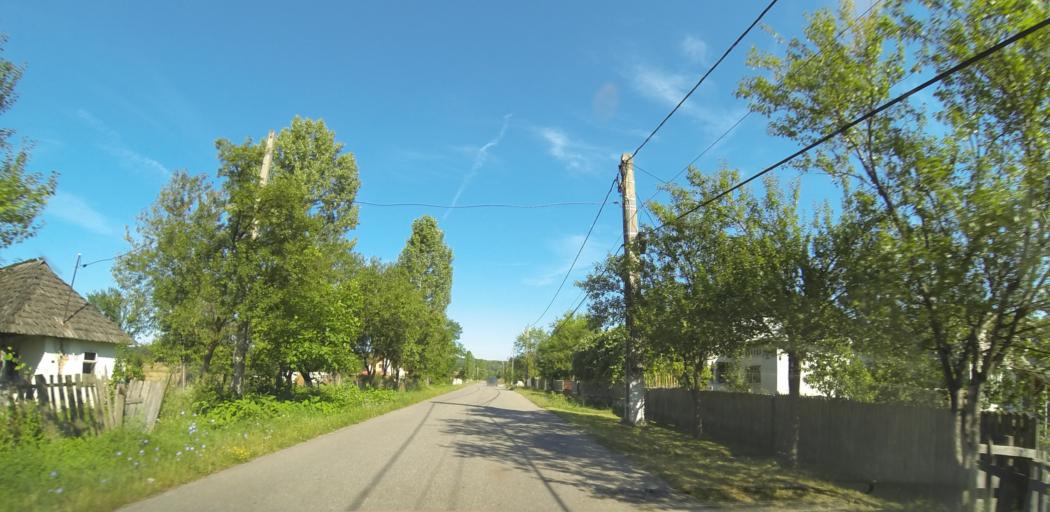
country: RO
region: Valcea
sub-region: Comuna Slatioara
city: Slatioara
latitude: 45.1325
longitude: 23.8793
